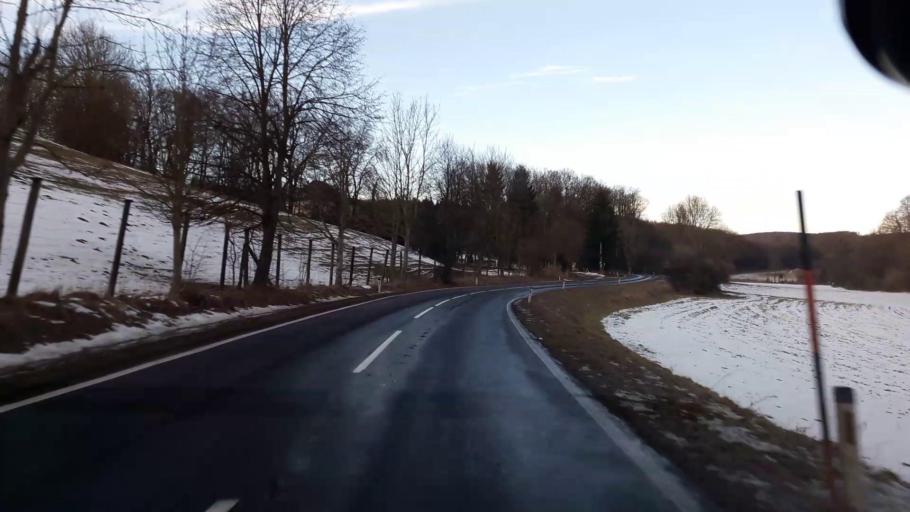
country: AT
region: Lower Austria
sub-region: Politischer Bezirk Wien-Umgebung
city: Mauerbach
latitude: 48.2526
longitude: 16.1649
